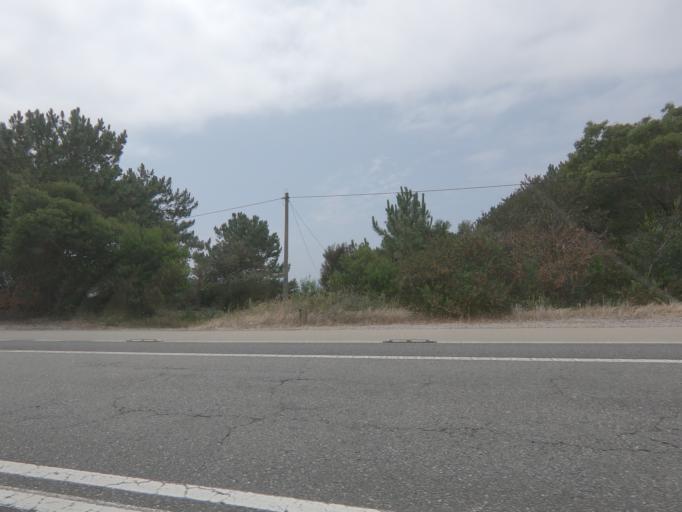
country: ES
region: Galicia
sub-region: Provincia de Pontevedra
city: Oia
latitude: 41.9751
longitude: -8.8845
